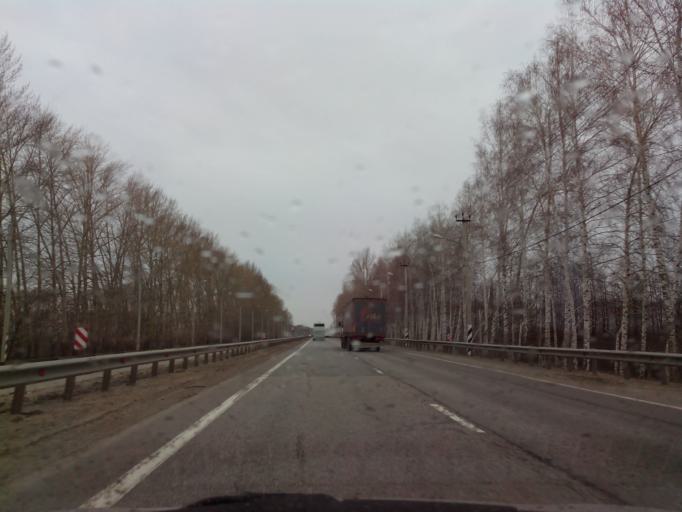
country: RU
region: Tambov
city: Selezni
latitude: 52.7551
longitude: 41.1625
